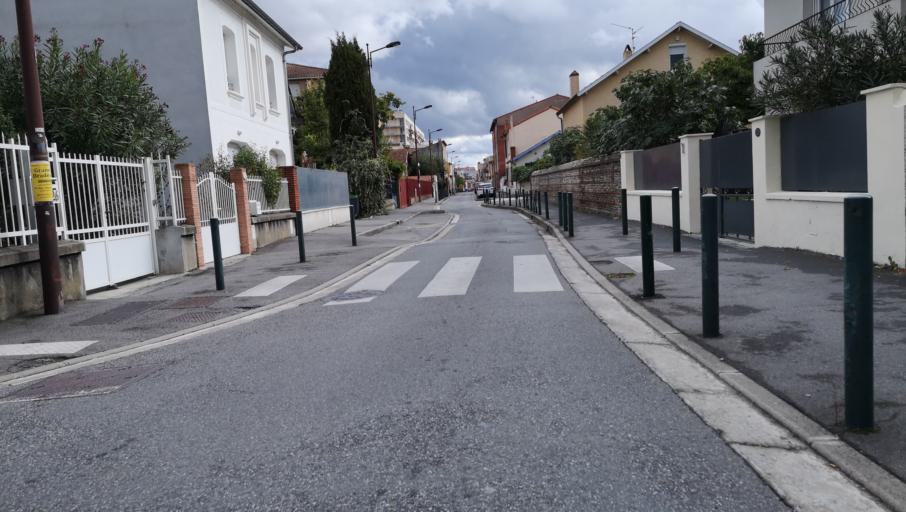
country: FR
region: Midi-Pyrenees
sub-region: Departement de la Haute-Garonne
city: Toulouse
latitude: 43.6026
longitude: 1.4121
